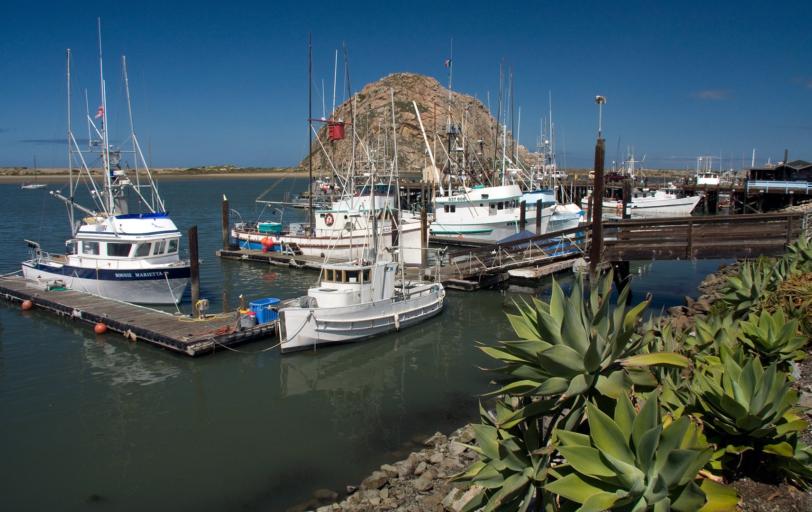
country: US
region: California
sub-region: San Luis Obispo County
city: Morro Bay
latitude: 35.3690
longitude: -120.8546
